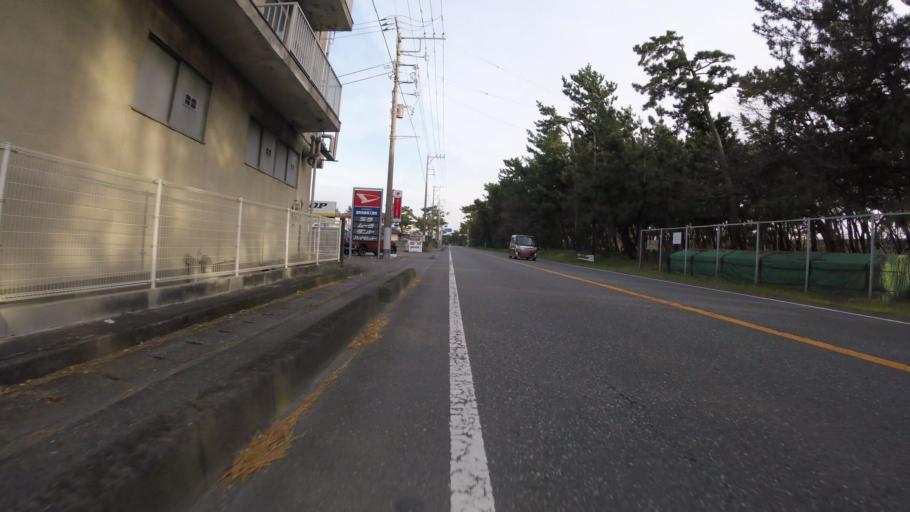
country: JP
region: Shizuoka
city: Fuji
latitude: 35.1332
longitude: 138.7542
